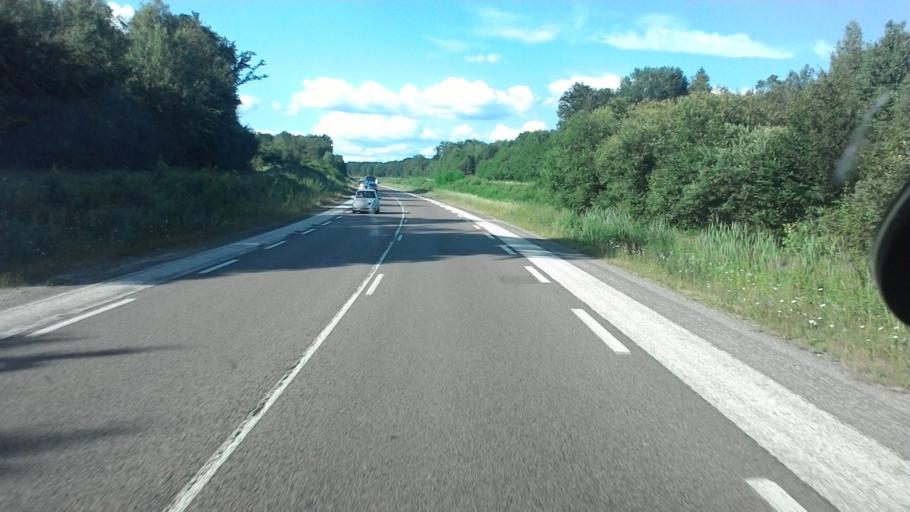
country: FR
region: Franche-Comte
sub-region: Departement de la Haute-Saone
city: Saint-Sauveur
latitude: 47.7922
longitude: 6.4006
